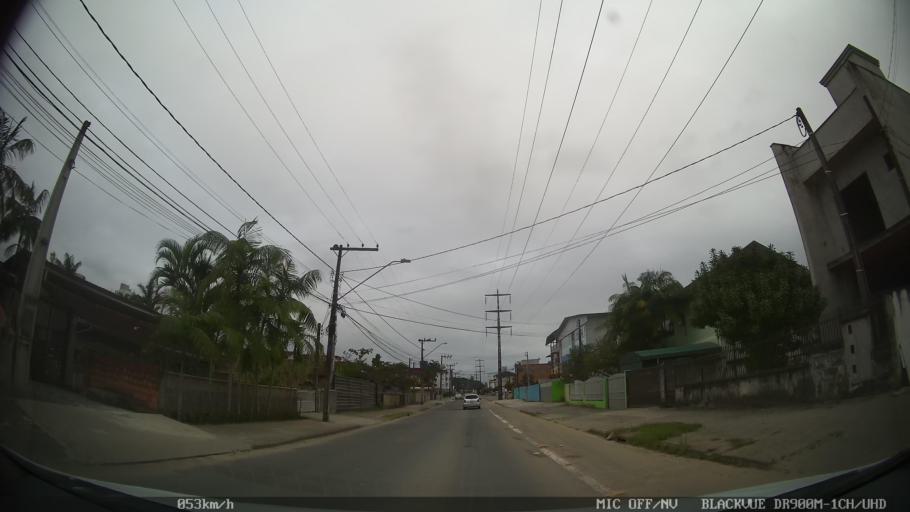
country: BR
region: Santa Catarina
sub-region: Joinville
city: Joinville
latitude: -26.2810
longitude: -48.8756
